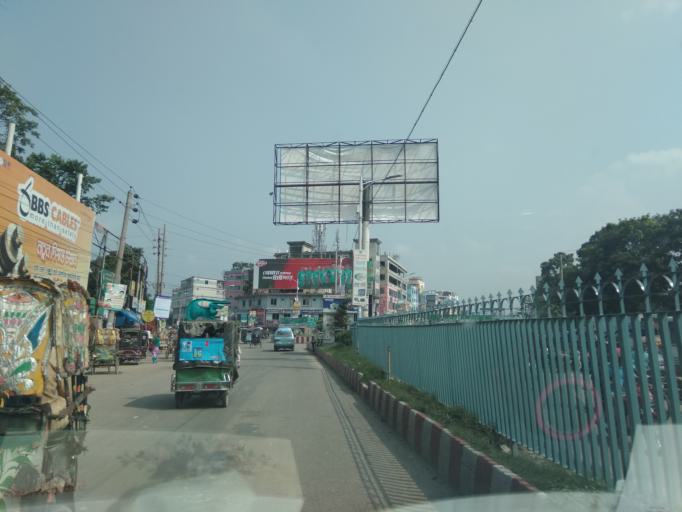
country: BD
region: Rangpur Division
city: Rangpur
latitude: 25.7658
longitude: 89.2311
